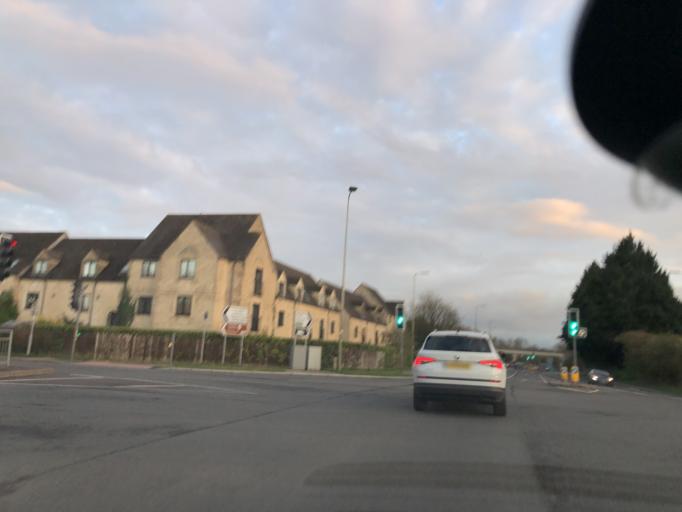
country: GB
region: England
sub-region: Oxfordshire
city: Witney
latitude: 51.7775
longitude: -1.4929
